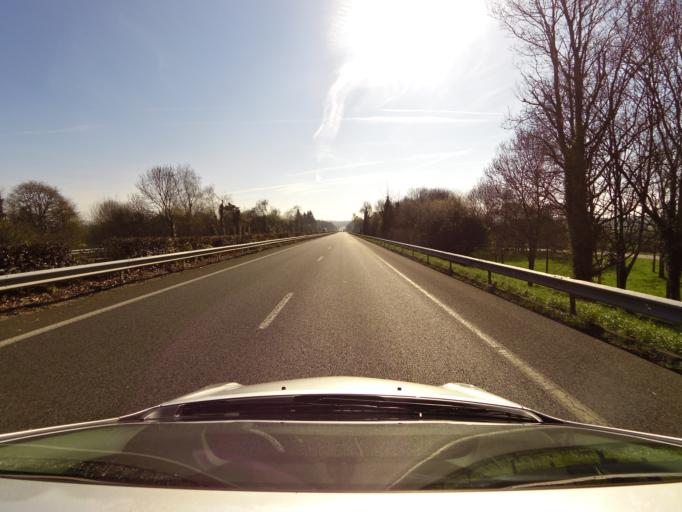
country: FR
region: Brittany
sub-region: Departement du Morbihan
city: Taupont
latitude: 47.9366
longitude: -2.4467
